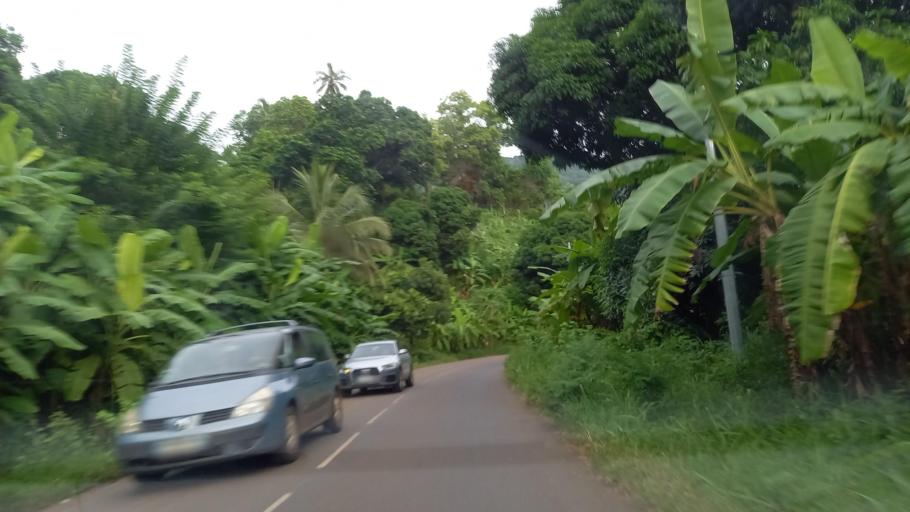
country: YT
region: Sada
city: Sada
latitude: -12.8630
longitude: 45.1114
